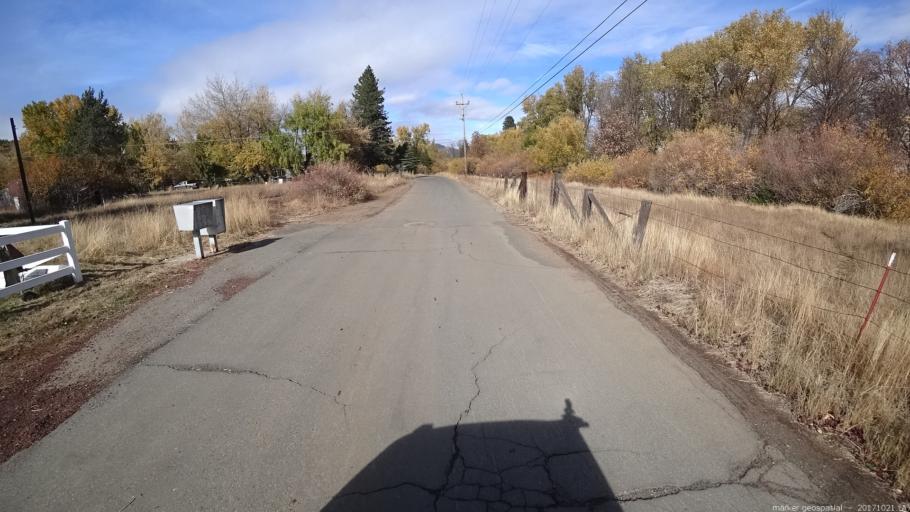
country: US
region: California
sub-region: Shasta County
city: Burney
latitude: 40.8881
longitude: -121.6691
